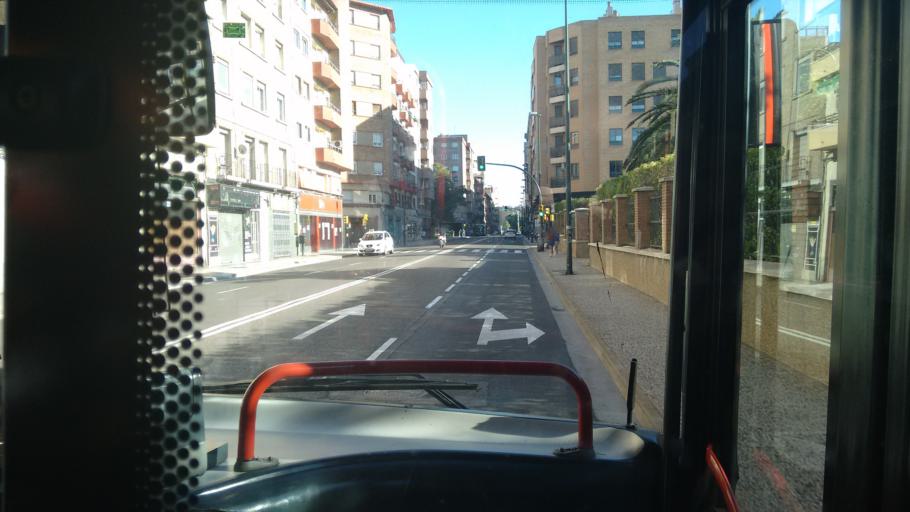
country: ES
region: Aragon
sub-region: Provincia de Zaragoza
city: Zaragoza
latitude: 41.6456
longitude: -0.8728
